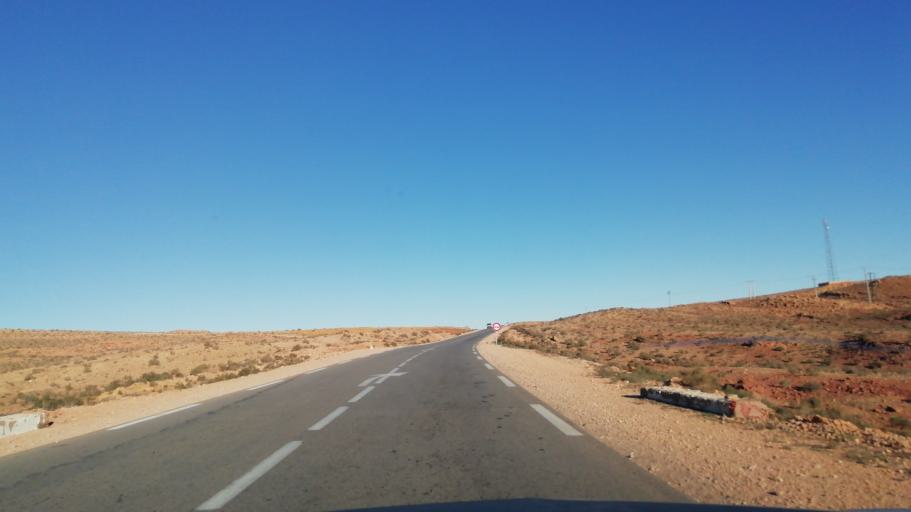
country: DZ
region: El Bayadh
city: El Abiodh Sidi Cheikh
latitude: 33.1721
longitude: 0.4398
